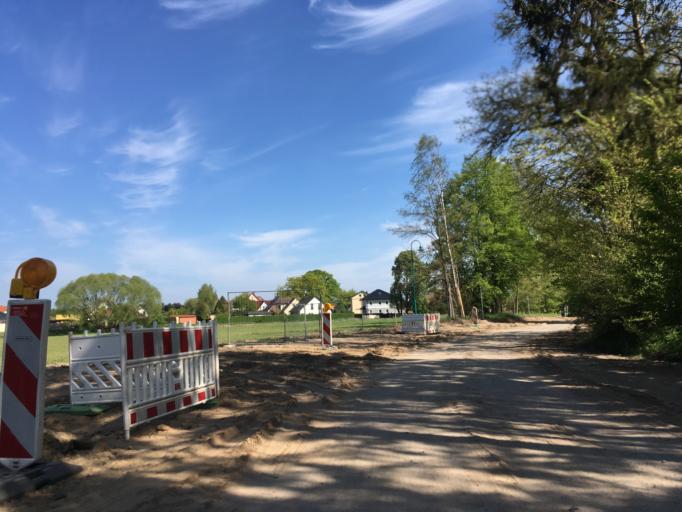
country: DE
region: Brandenburg
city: Rudnitz
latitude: 52.7241
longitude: 13.6155
